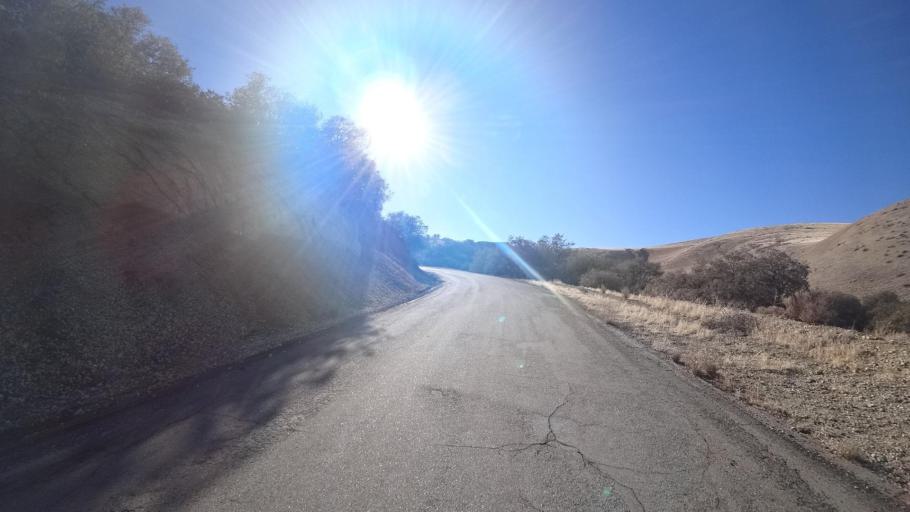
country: US
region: California
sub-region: Kern County
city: Maricopa
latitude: 34.9453
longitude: -119.4011
